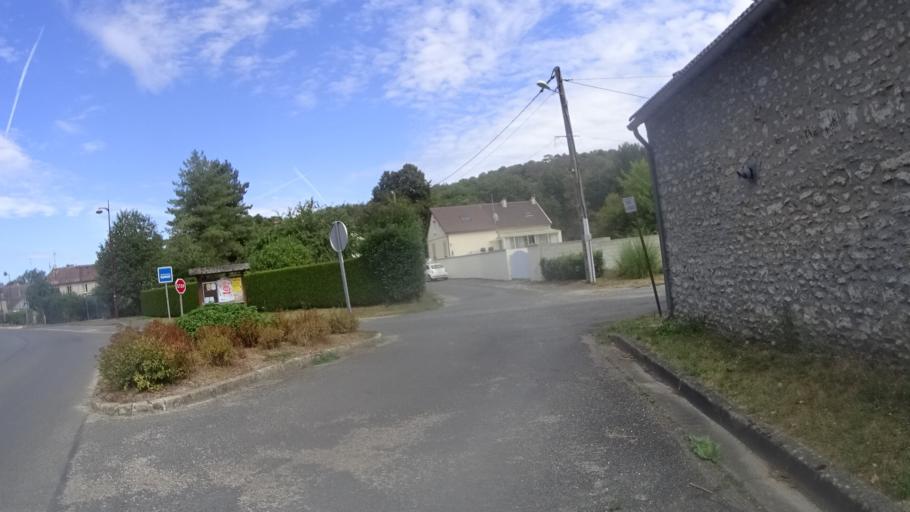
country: FR
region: Centre
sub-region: Departement du Loiret
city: Malesherbes
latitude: 48.2775
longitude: 2.4264
